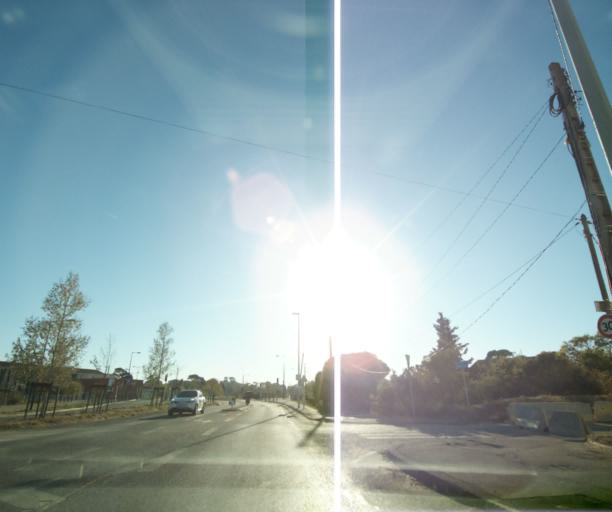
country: FR
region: Provence-Alpes-Cote d'Azur
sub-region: Departement des Bouches-du-Rhone
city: Plan-de-Cuques
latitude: 43.3437
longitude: 5.4462
